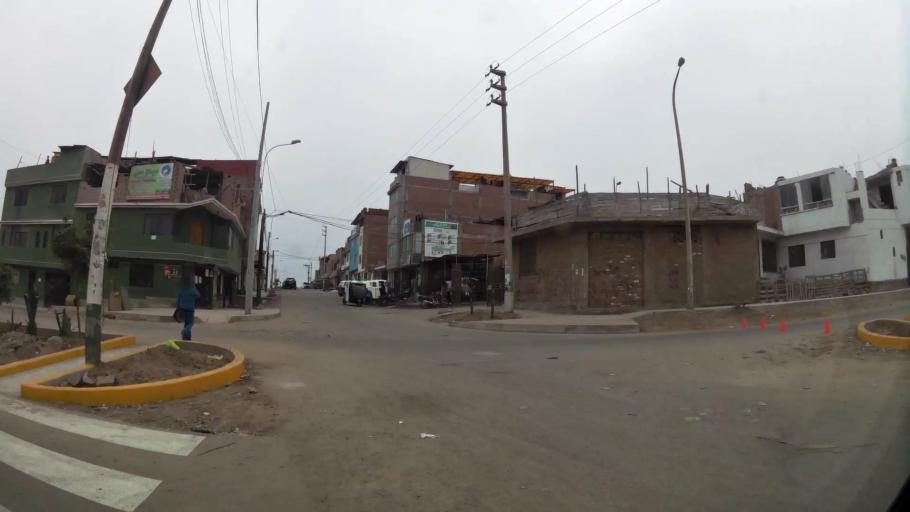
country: PE
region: Lima
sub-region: Lima
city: Surco
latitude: -12.1994
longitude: -76.9772
